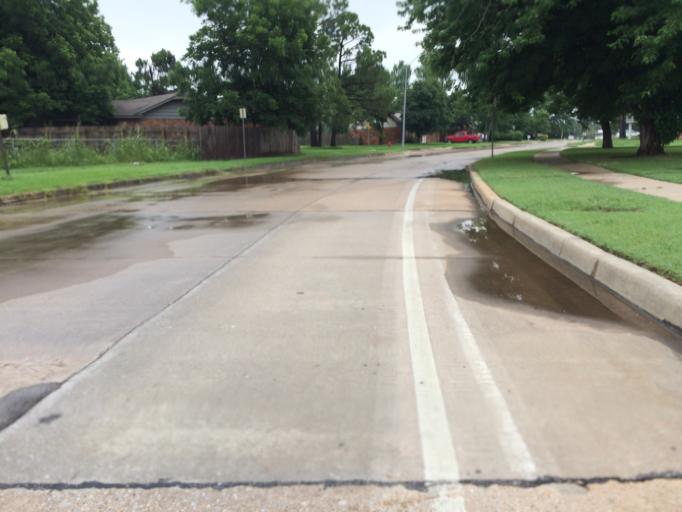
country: US
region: Oklahoma
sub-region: Cleveland County
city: Hall Park
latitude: 35.2107
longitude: -97.4132
